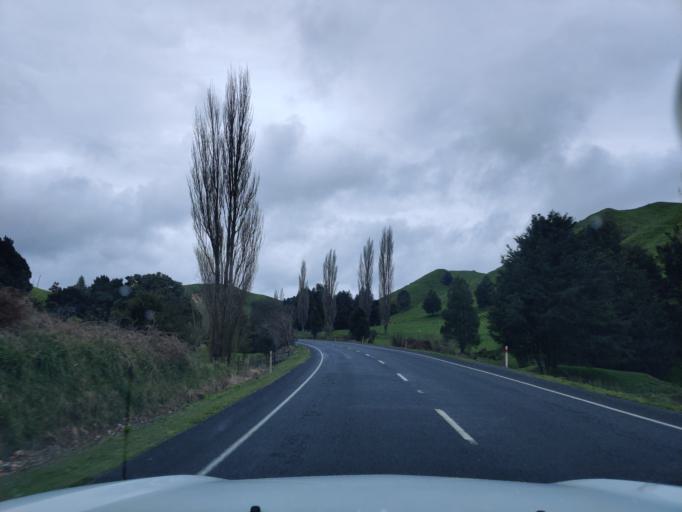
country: NZ
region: Waikato
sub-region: Otorohanga District
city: Otorohanga
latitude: -38.5686
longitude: 175.2062
